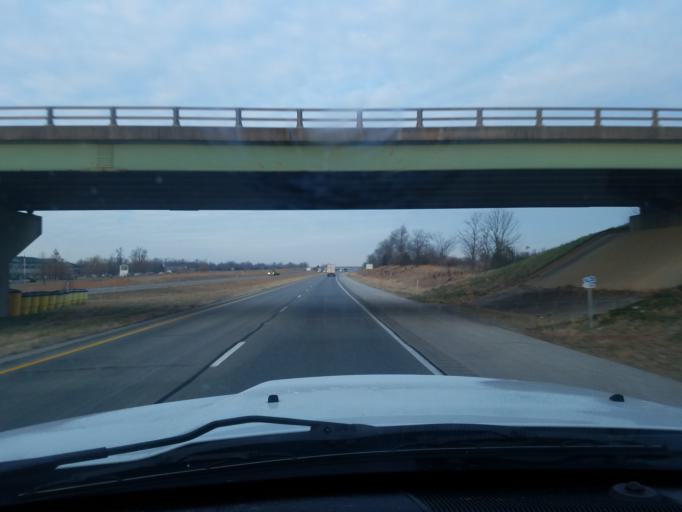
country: US
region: Indiana
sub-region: Harrison County
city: Corydon
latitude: 38.2394
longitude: -86.1446
